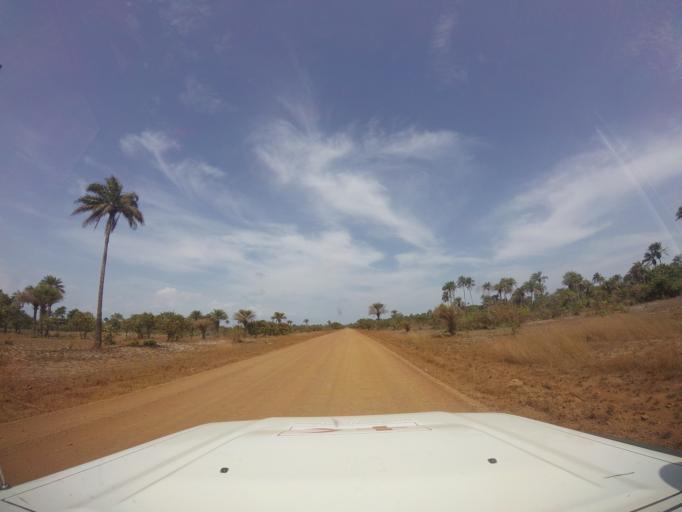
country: LR
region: Grand Cape Mount
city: Robertsport
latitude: 6.7030
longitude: -11.3195
